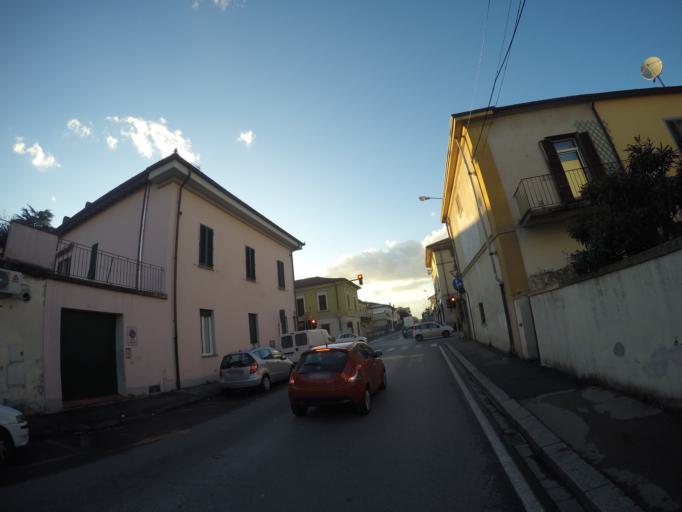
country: IT
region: Tuscany
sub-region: Provincia di Prato
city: Prato
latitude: 43.8840
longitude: 11.0929
